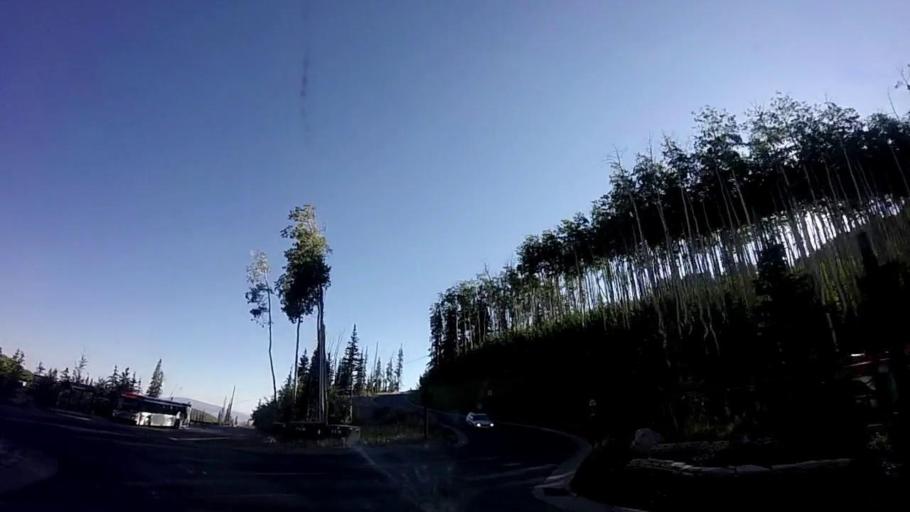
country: US
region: Utah
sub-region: Summit County
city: Park City
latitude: 40.6152
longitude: -111.5092
